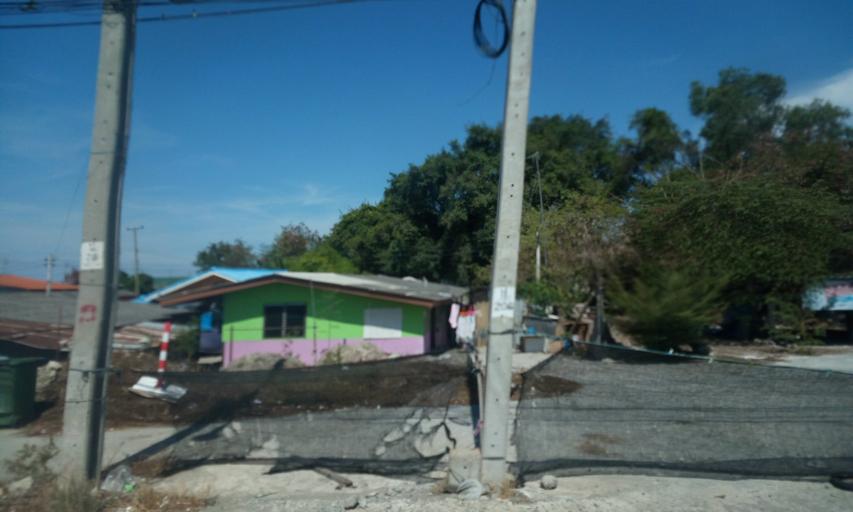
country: TH
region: Samut Prakan
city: Bang Bo District
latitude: 13.5401
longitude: 100.7884
